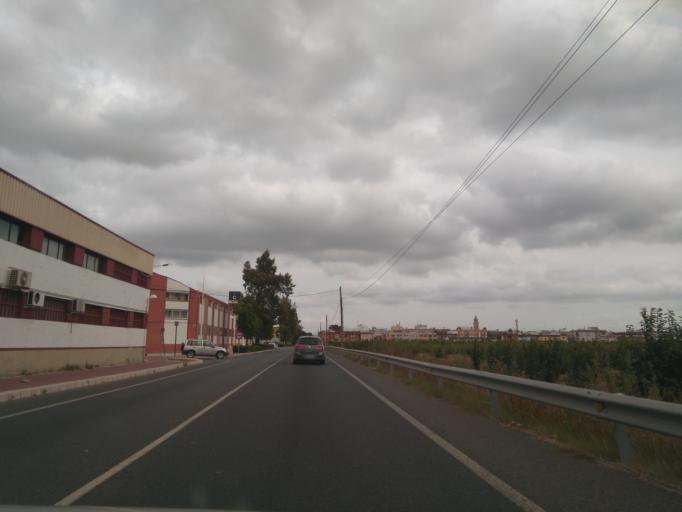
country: ES
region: Valencia
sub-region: Provincia de Valencia
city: L'Alcudia
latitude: 39.2052
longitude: -0.5084
